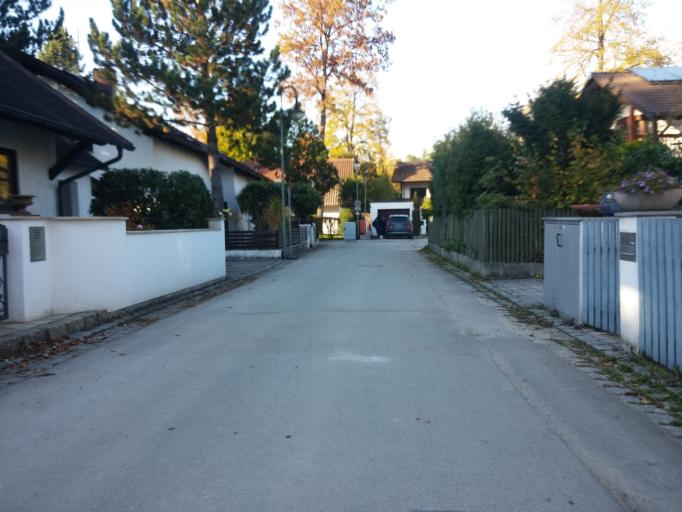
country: DE
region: Bavaria
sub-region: Upper Bavaria
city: Vaterstetten
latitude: 48.0992
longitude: 11.7820
